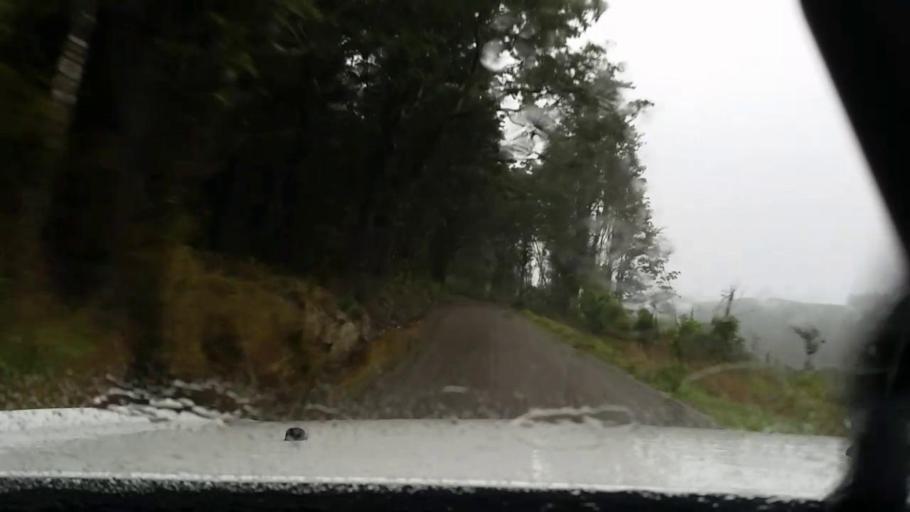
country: NZ
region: Wellington
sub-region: Masterton District
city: Masterton
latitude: -41.1841
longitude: 175.8230
